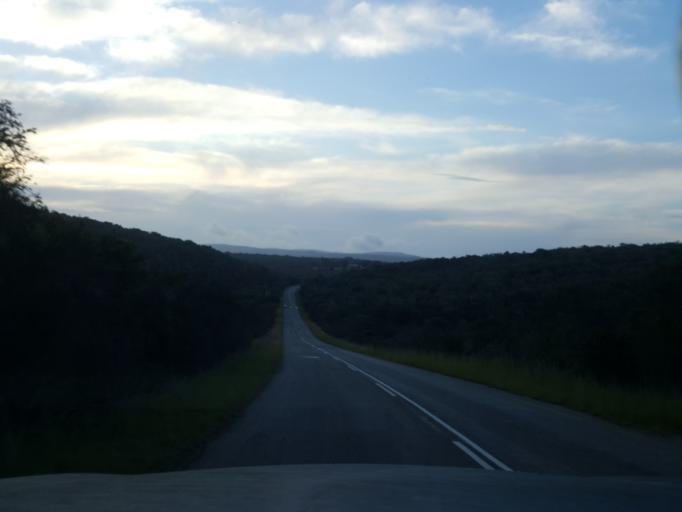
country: ZA
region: Eastern Cape
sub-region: Cacadu District Municipality
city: Grahamstown
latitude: -33.4068
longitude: 26.4767
